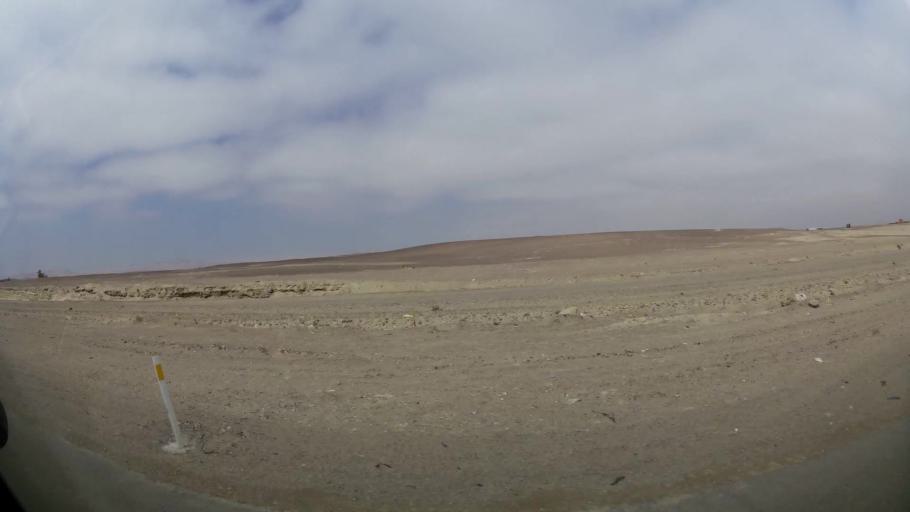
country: PE
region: Ica
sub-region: Provincia de Pisco
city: Independencia
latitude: -13.9096
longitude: -76.0172
